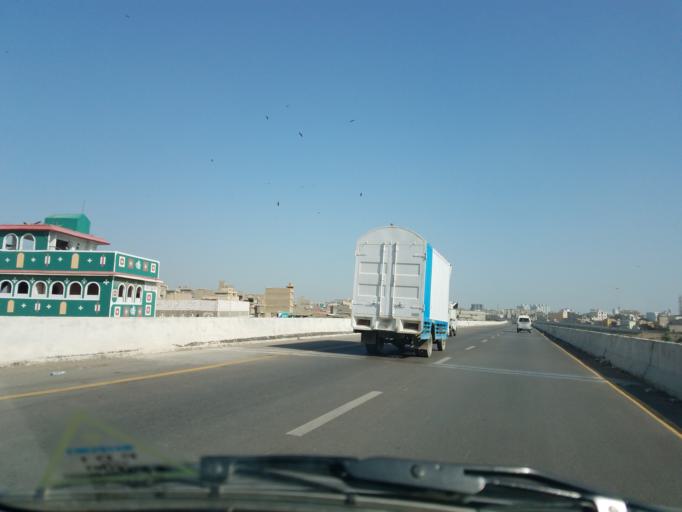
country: PK
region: Sindh
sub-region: Karachi District
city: Karachi
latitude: 24.8819
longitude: 67.0058
